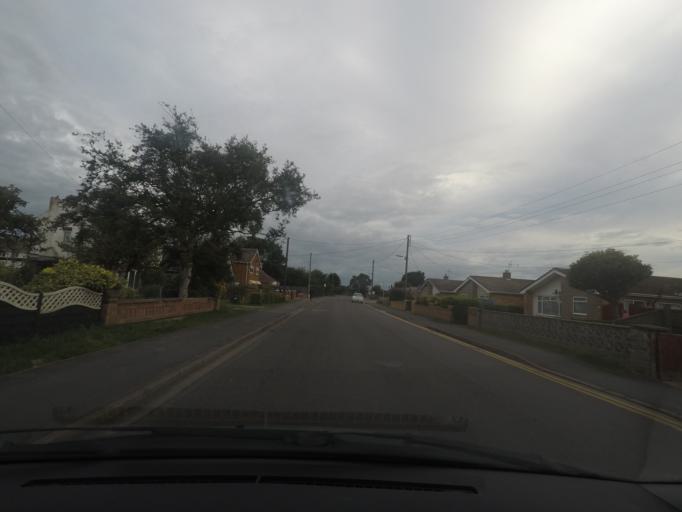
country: GB
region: England
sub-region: Lincolnshire
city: Chapel Saint Leonards
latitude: 53.2209
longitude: 0.3361
